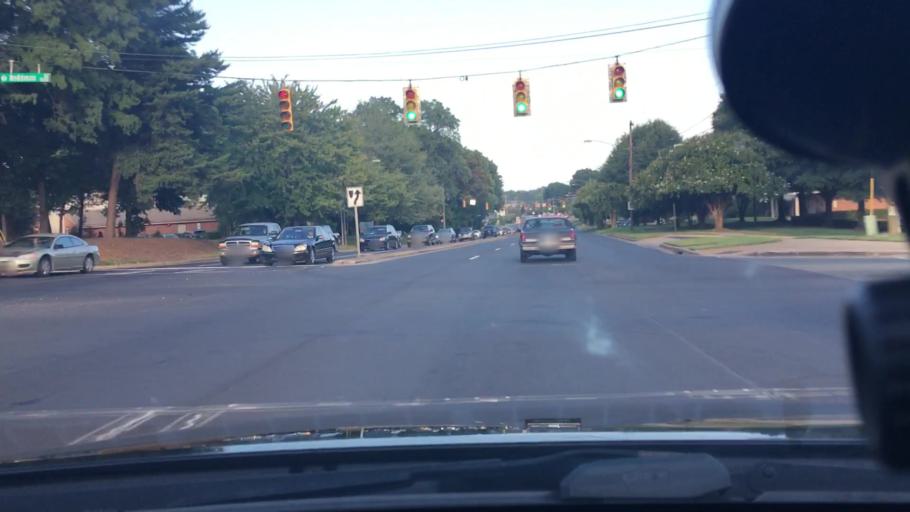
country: US
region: North Carolina
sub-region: Mecklenburg County
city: Matthews
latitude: 35.2039
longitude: -80.7505
